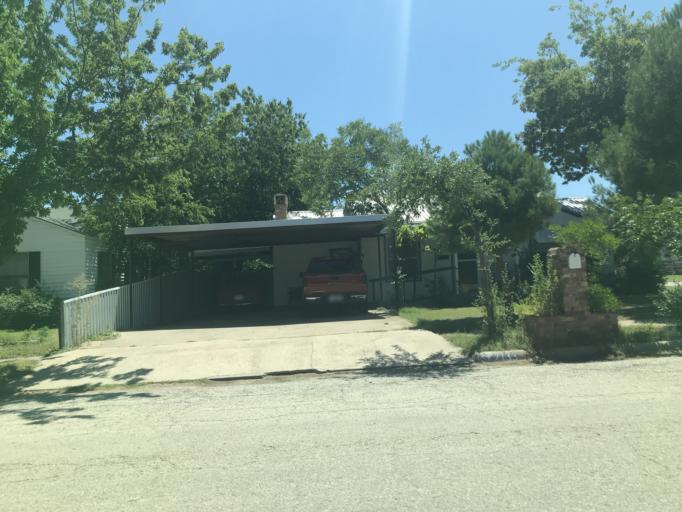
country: US
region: Texas
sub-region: Taylor County
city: Abilene
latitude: 32.4224
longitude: -99.7424
